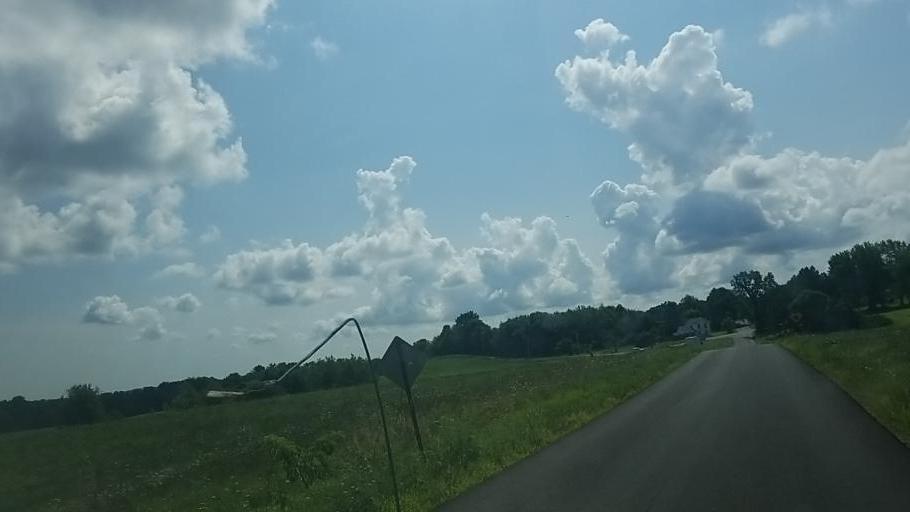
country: US
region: Ohio
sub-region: Richland County
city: Lincoln Heights
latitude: 40.6842
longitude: -82.3805
